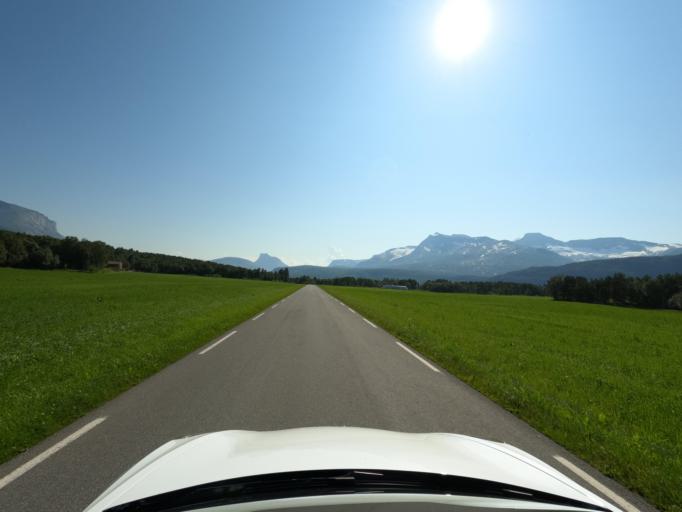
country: NO
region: Nordland
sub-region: Narvik
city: Narvik
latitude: 68.3234
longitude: 17.2889
